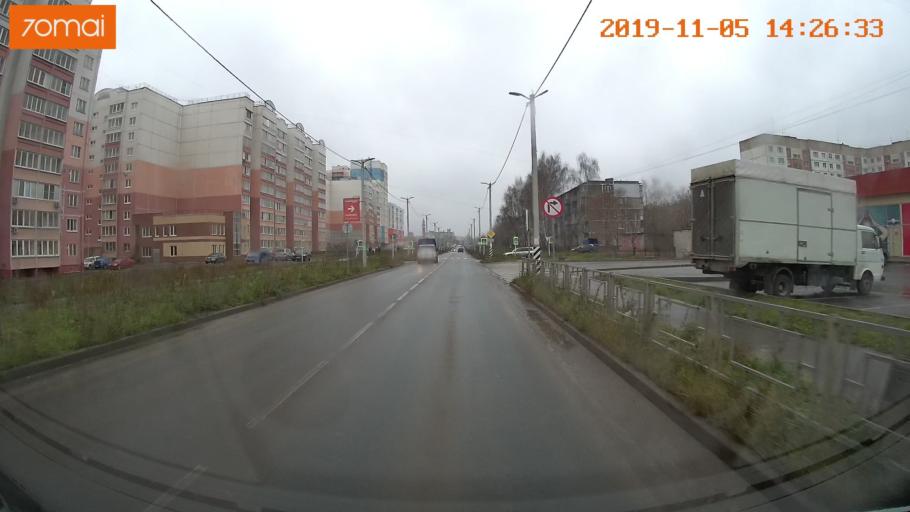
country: RU
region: Ivanovo
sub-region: Gorod Ivanovo
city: Ivanovo
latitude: 56.9698
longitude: 40.9849
